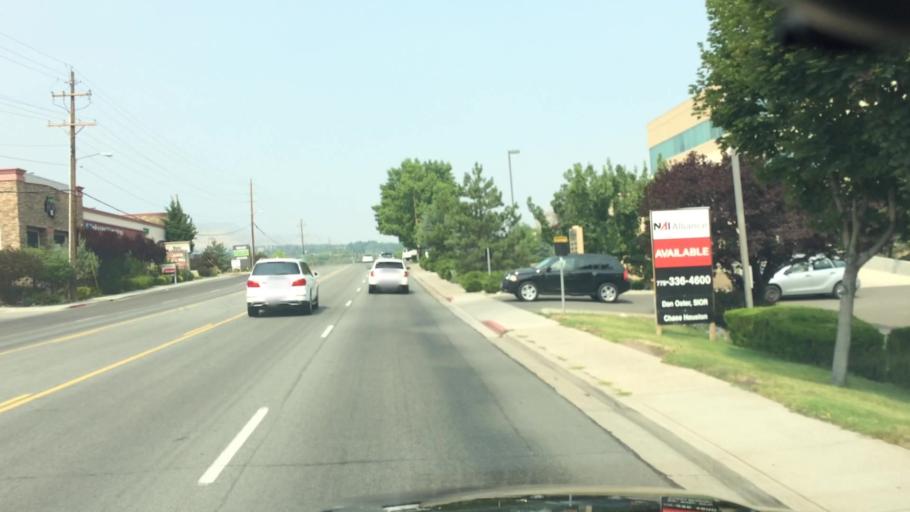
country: US
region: Nevada
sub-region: Washoe County
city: Reno
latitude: 39.4913
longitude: -119.8038
